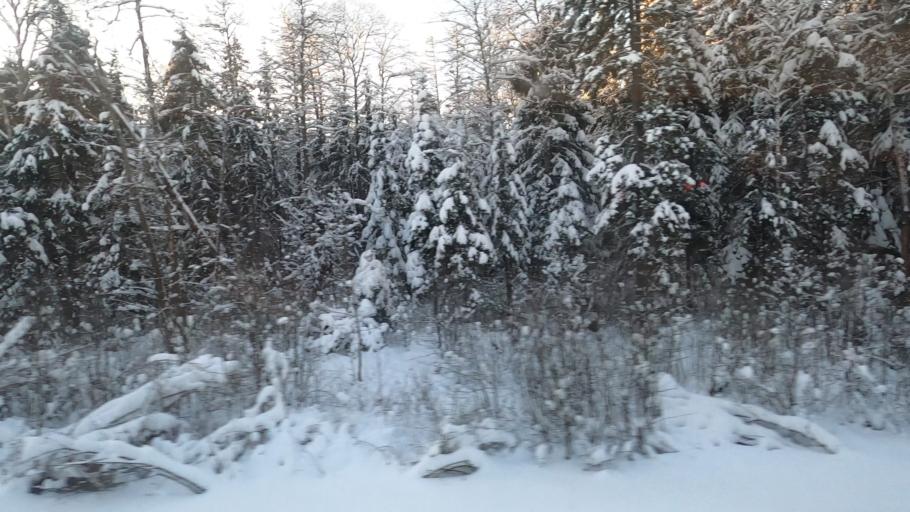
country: RU
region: Moskovskaya
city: Novo-Nikol'skoye
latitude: 56.5964
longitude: 37.5665
